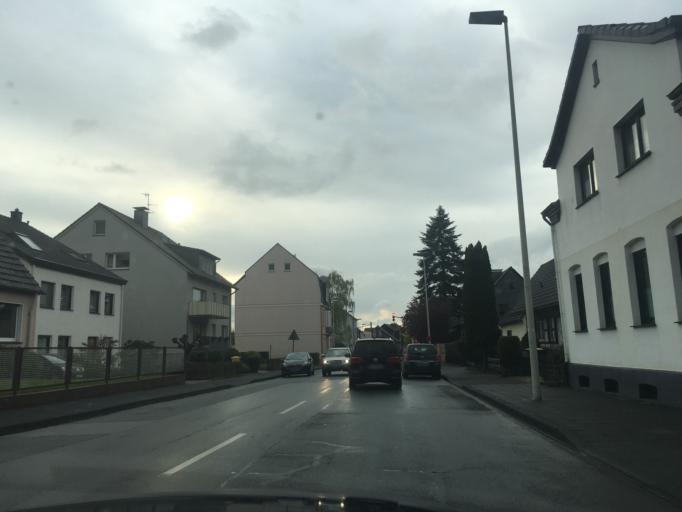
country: DE
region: North Rhine-Westphalia
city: Leichlingen
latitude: 51.1497
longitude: 7.0161
